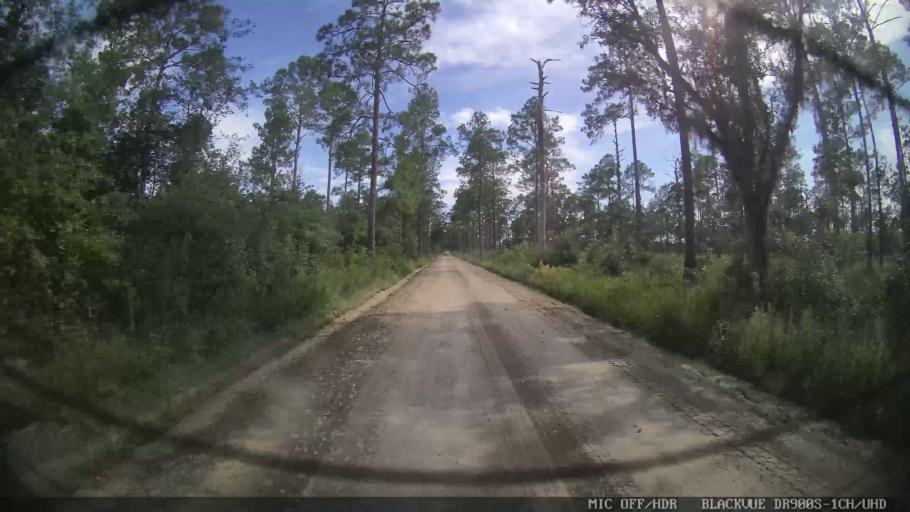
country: US
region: Georgia
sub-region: Echols County
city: Statenville
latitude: 30.6242
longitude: -83.1995
